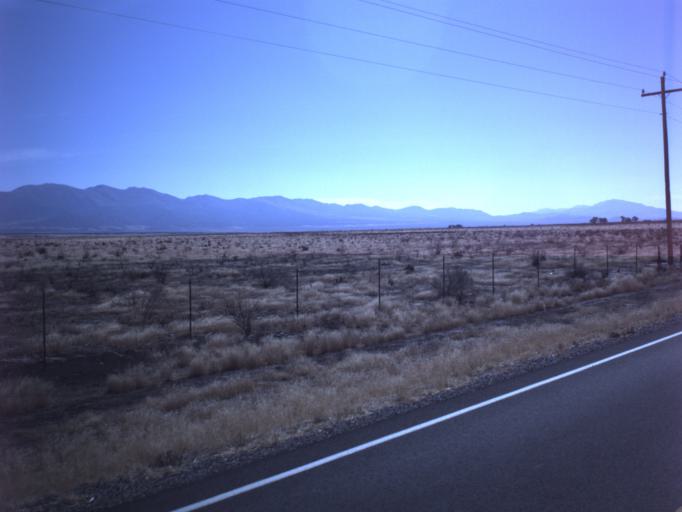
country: US
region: Utah
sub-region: Tooele County
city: Grantsville
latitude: 40.3617
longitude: -112.7459
